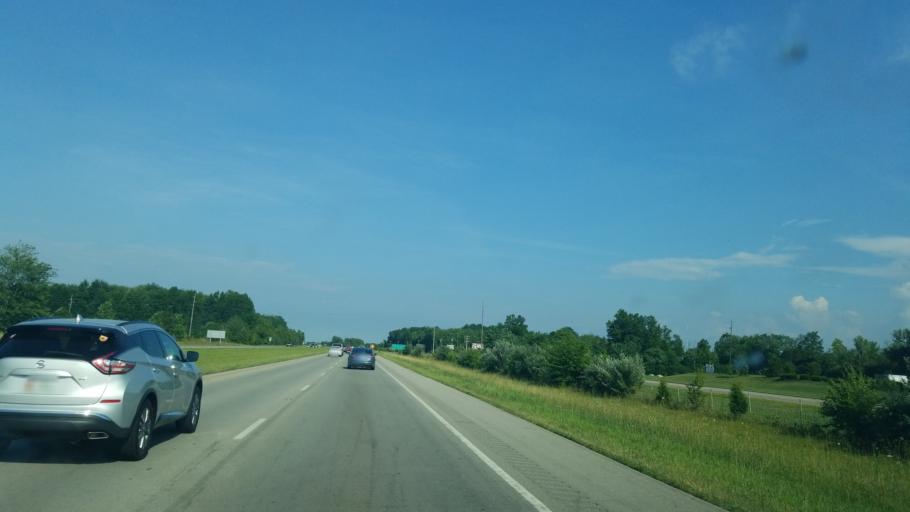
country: US
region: Ohio
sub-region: Clermont County
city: Williamsburg
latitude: 39.0735
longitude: -84.1126
